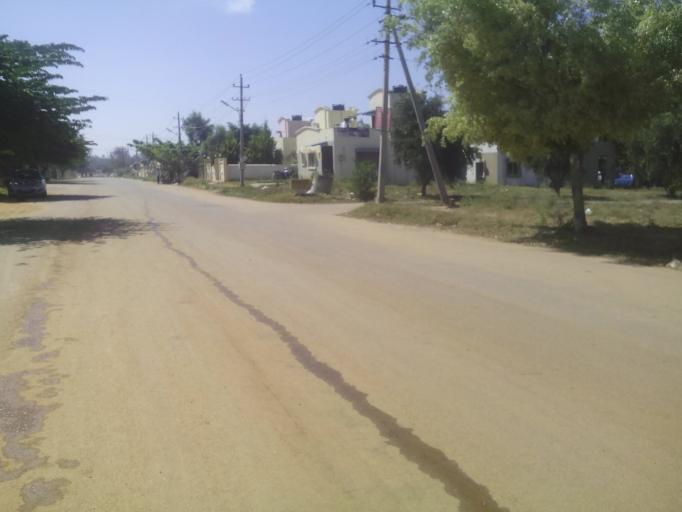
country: IN
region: Karnataka
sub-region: Bangalore Urban
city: Anekal
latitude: 12.7897
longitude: 77.7016
